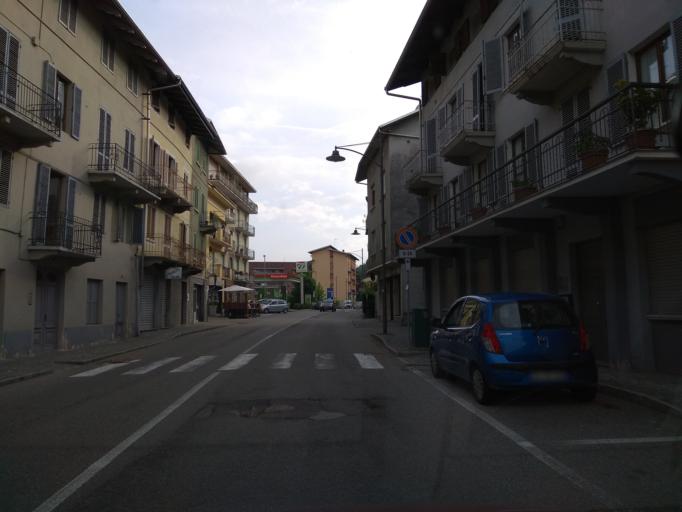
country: IT
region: Piedmont
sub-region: Provincia di Biella
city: Trivero-Prativero-Ponzone
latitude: 45.6545
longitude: 8.1874
